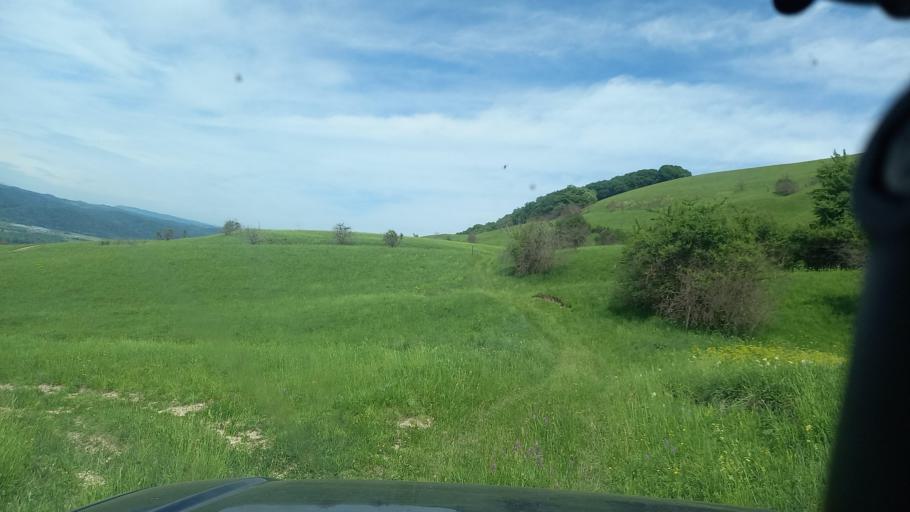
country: RU
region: Karachayevo-Cherkesiya
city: Kurdzhinovo
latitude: 44.1482
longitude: 41.0711
